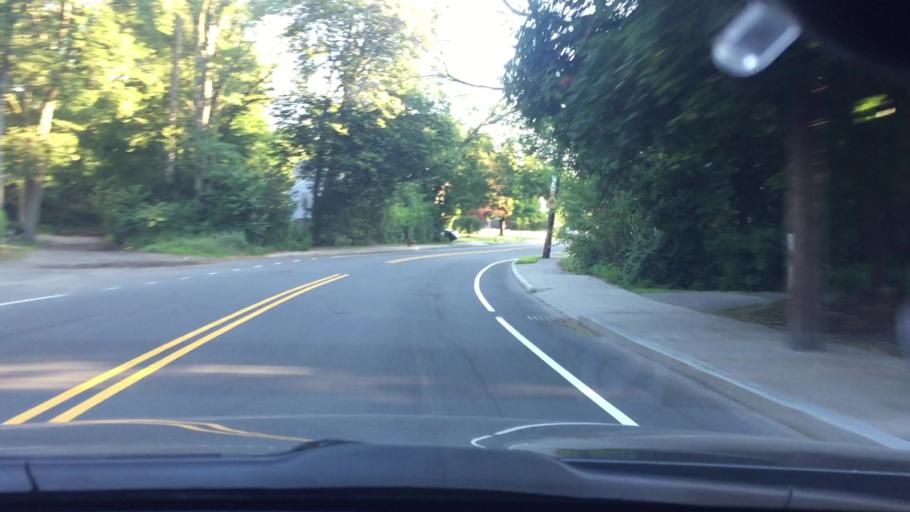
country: US
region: Massachusetts
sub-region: Middlesex County
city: Newton
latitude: 42.3124
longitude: -71.2091
